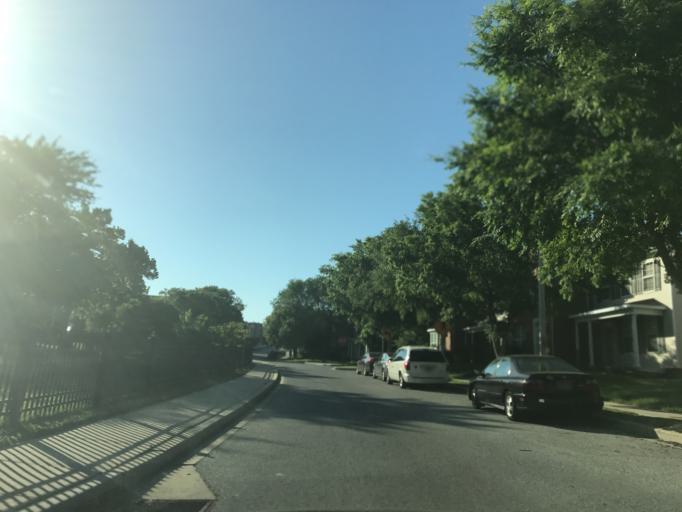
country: US
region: Maryland
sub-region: City of Baltimore
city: Baltimore
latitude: 39.2961
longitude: -76.6289
